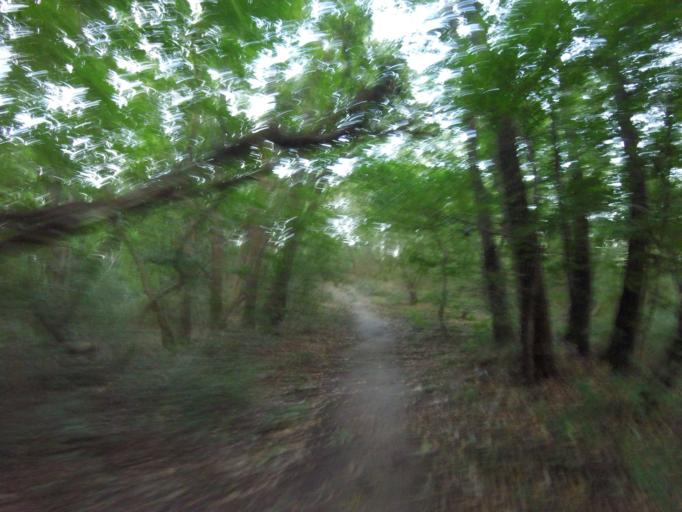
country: HU
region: Pest
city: Fot
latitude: 47.6273
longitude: 19.2144
